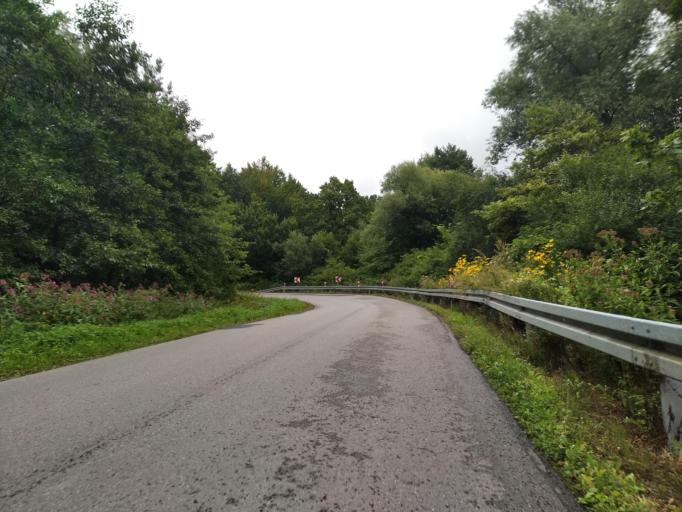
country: PL
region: Subcarpathian Voivodeship
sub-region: Powiat brzozowski
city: Nozdrzec
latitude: 49.7254
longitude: 22.2977
